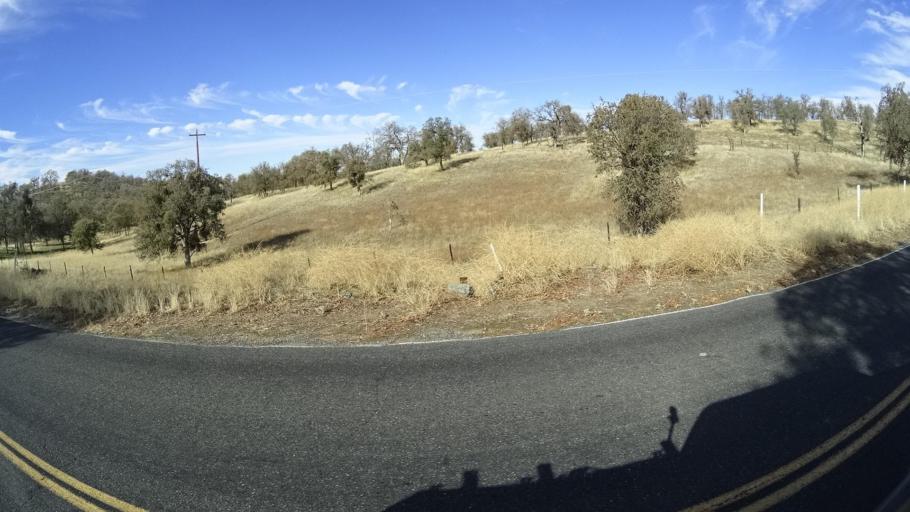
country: US
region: California
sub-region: Kern County
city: Alta Sierra
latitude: 35.6474
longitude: -118.7808
